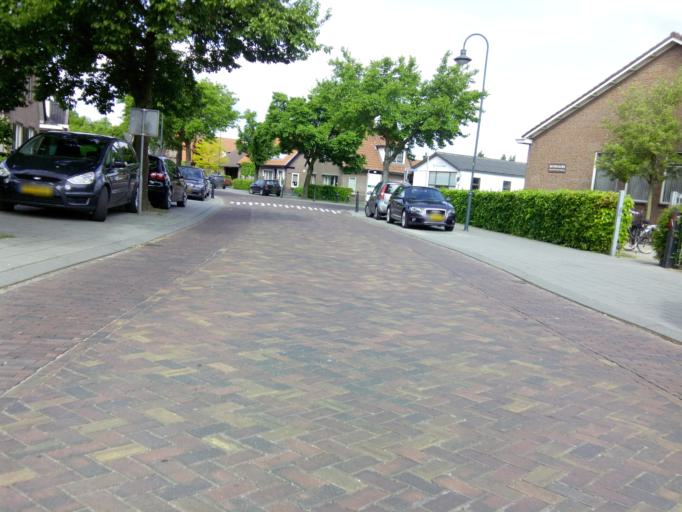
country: NL
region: Gelderland
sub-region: Gemeente Ede
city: Lunteren
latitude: 52.0868
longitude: 5.6171
